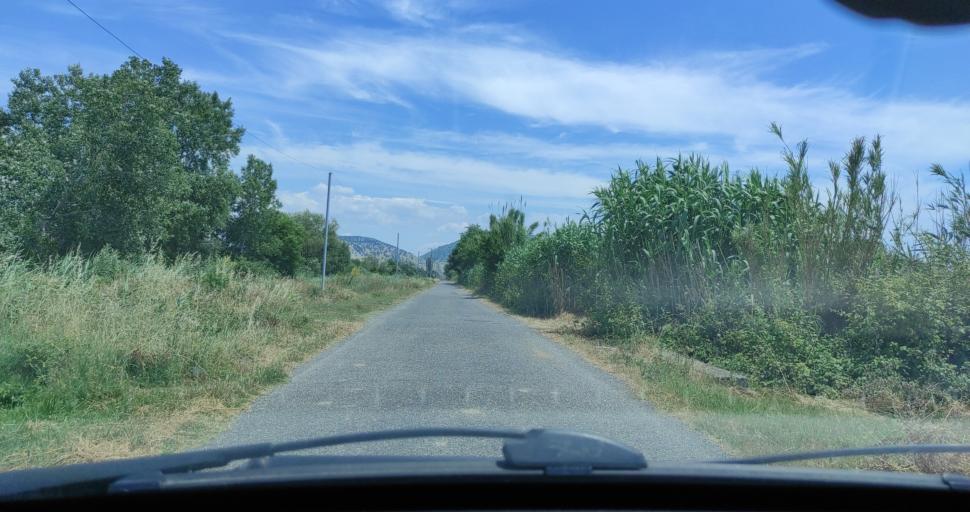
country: AL
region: Shkoder
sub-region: Rrethi i Shkodres
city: Velipoje
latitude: 41.8788
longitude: 19.3915
